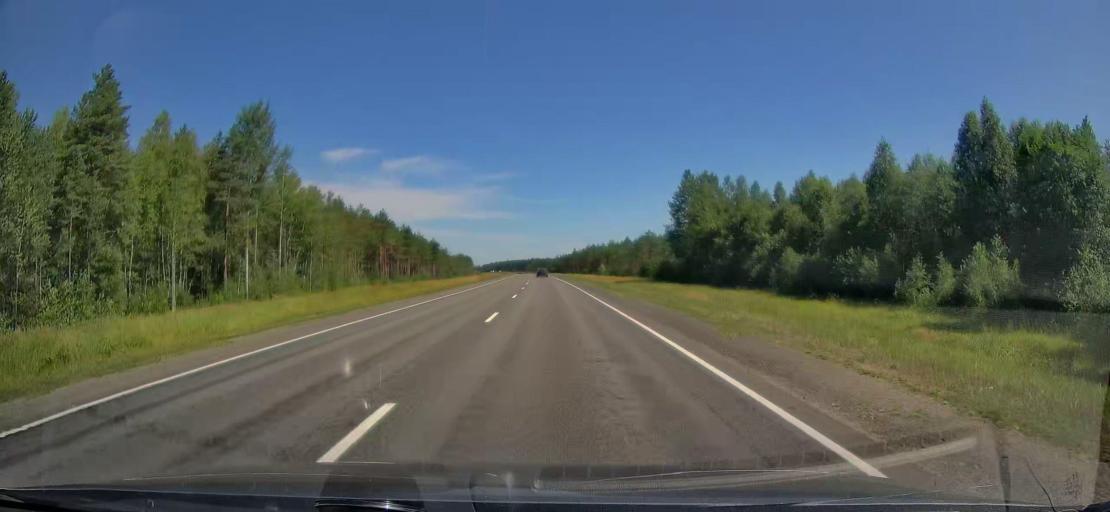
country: RU
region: Tverskaya
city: Ves'yegonsk
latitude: 58.9271
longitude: 37.2504
